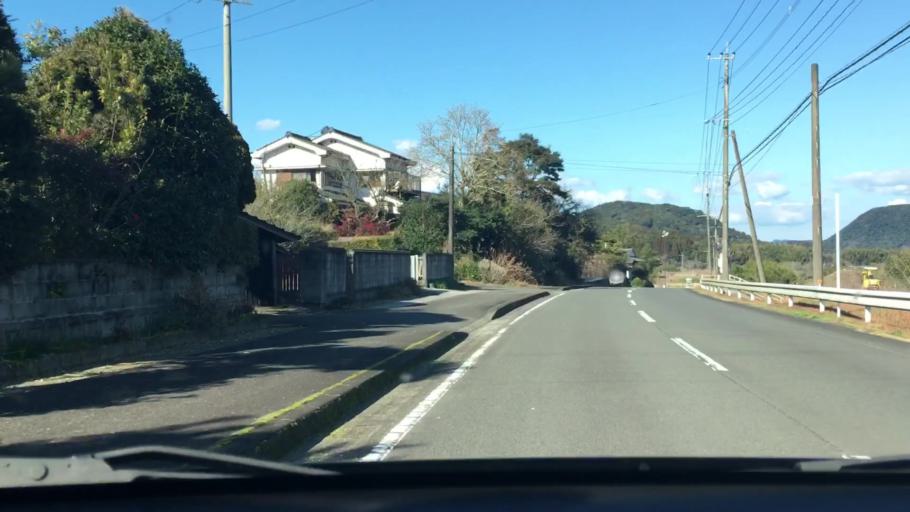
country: JP
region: Kagoshima
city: Satsumasendai
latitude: 31.7721
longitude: 130.4013
